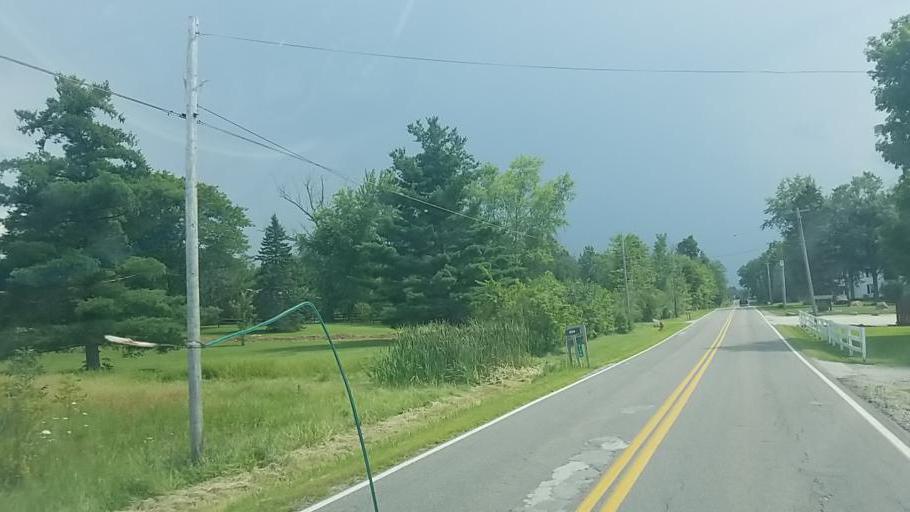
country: US
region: Ohio
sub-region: Medina County
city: Lodi
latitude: 41.0512
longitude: -82.0055
